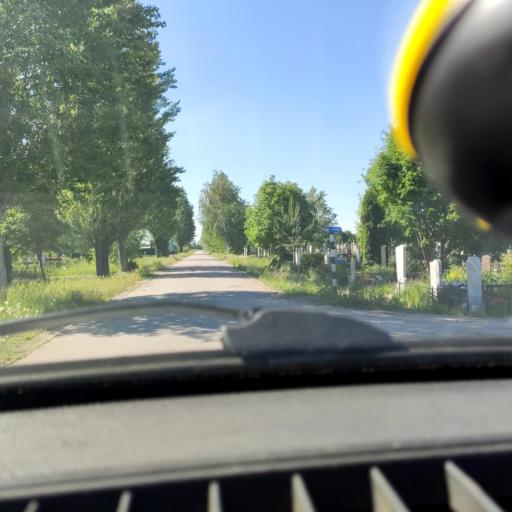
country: RU
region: Samara
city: Tol'yatti
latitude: 53.5750
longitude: 49.4274
